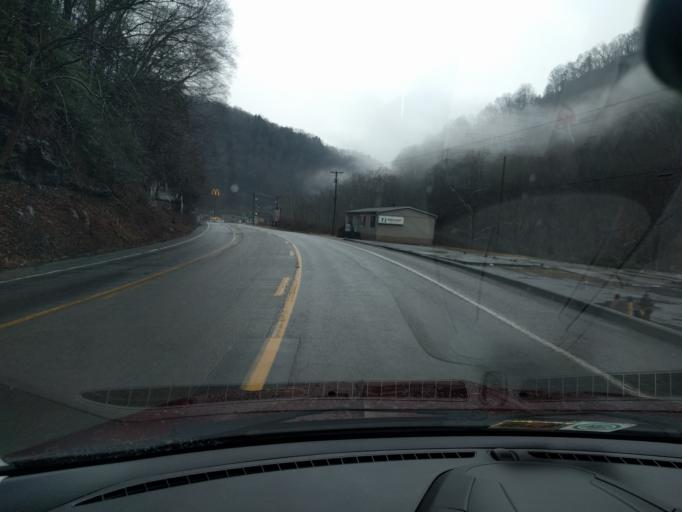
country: US
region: West Virginia
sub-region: McDowell County
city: Welch
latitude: 37.4326
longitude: -81.5653
